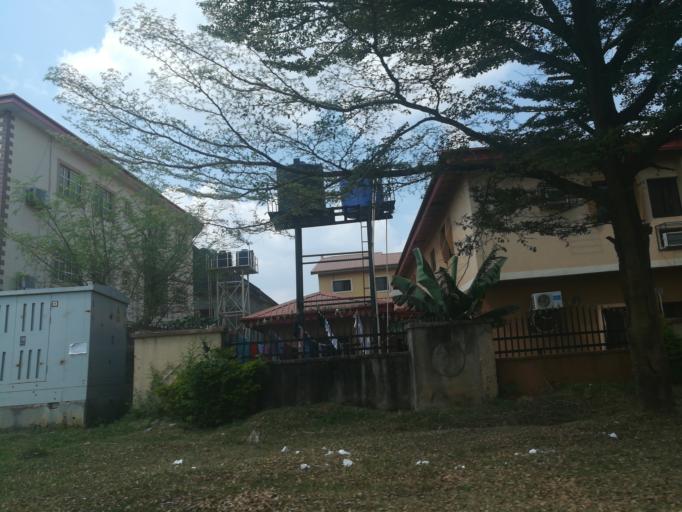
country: NG
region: Abuja Federal Capital Territory
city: Abuja
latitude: 9.0468
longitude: 7.4460
